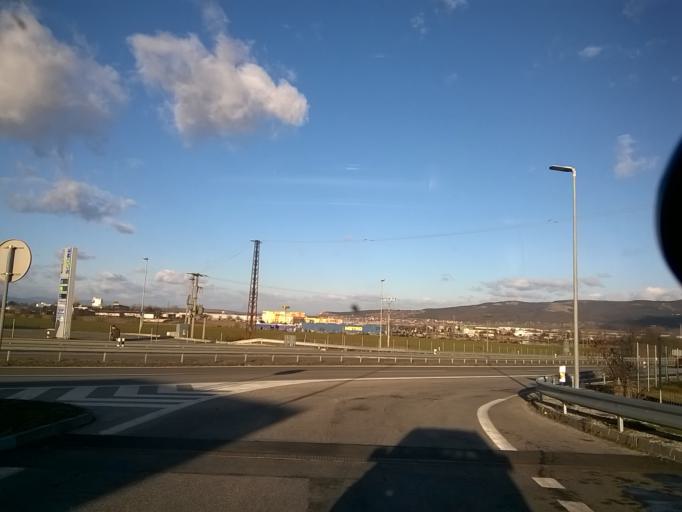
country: SK
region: Nitriansky
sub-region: Okres Nitra
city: Nitra
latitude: 48.3159
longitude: 18.0304
